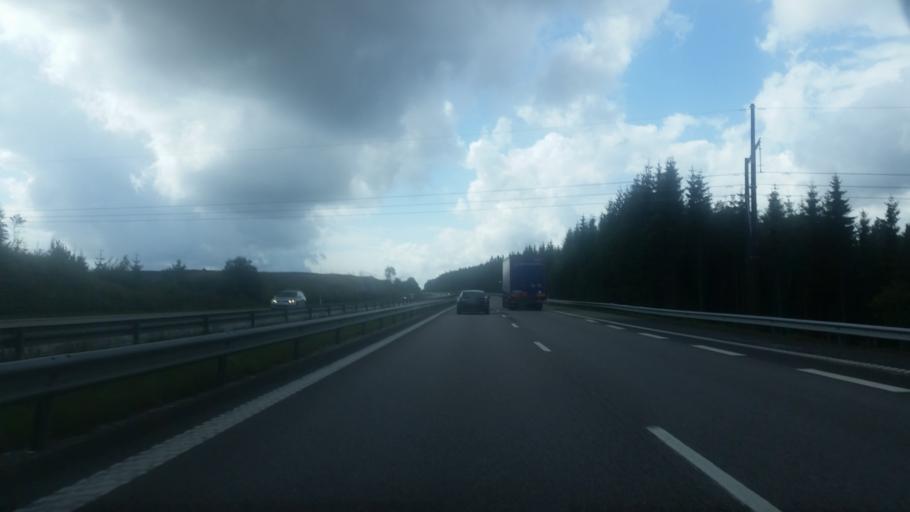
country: SE
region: Vaestra Goetaland
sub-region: Boras Kommun
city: Sandared
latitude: 57.6952
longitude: 12.8131
